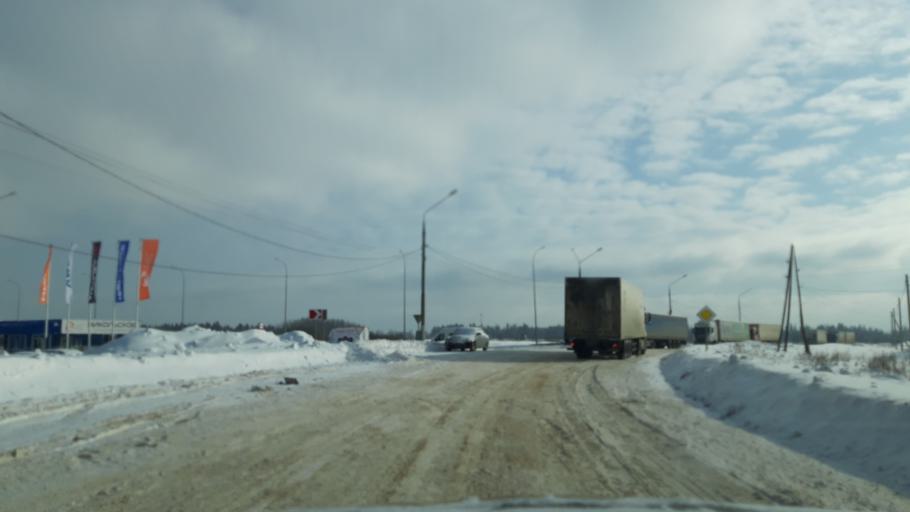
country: RU
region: Moskovskaya
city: Yermolino
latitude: 56.1422
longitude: 37.3794
